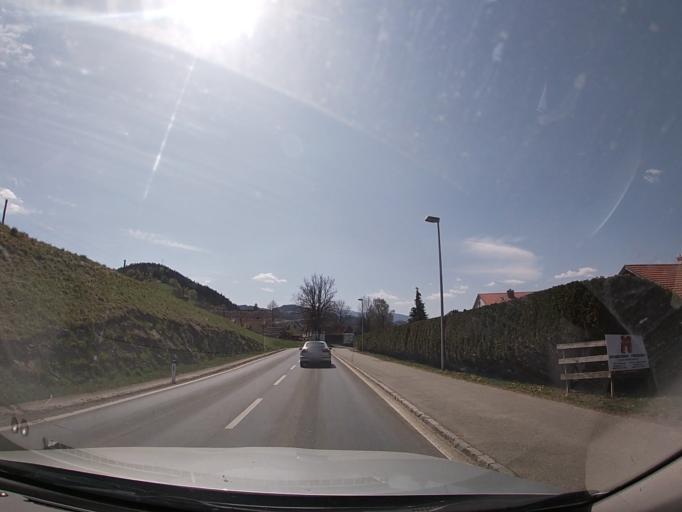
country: AT
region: Styria
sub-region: Politischer Bezirk Murtal
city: Sankt Margarethen bei Knittelfeld
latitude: 47.2180
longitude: 14.8489
